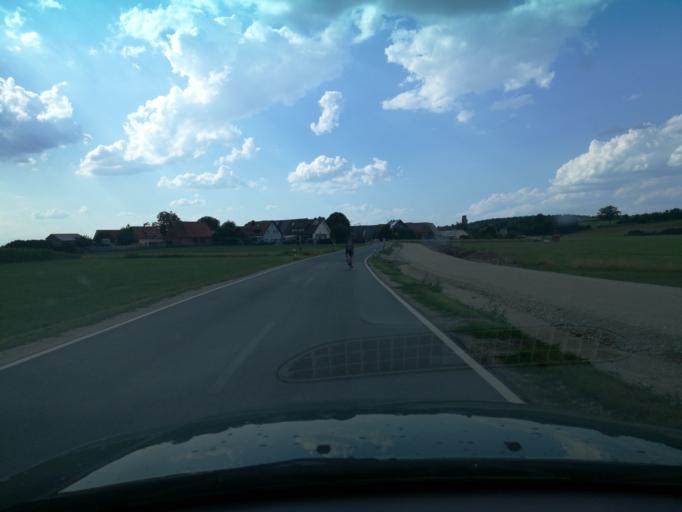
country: DE
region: Bavaria
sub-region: Regierungsbezirk Mittelfranken
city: Cadolzburg
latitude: 49.4815
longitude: 10.8536
